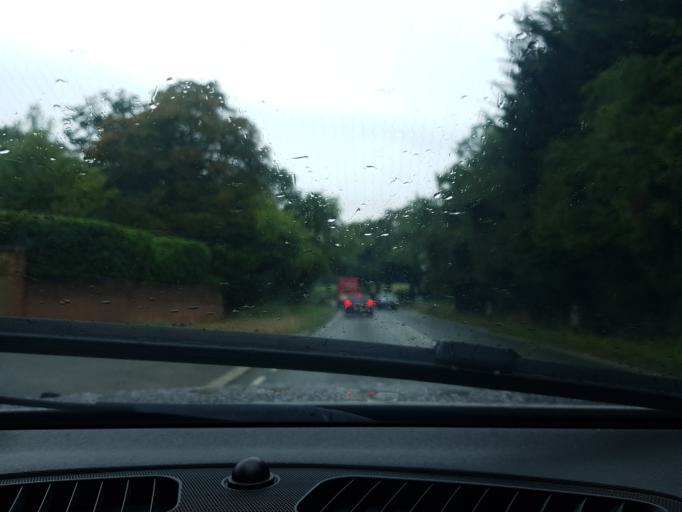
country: GB
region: England
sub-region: Hampshire
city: Fleet
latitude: 51.2450
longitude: -0.8498
